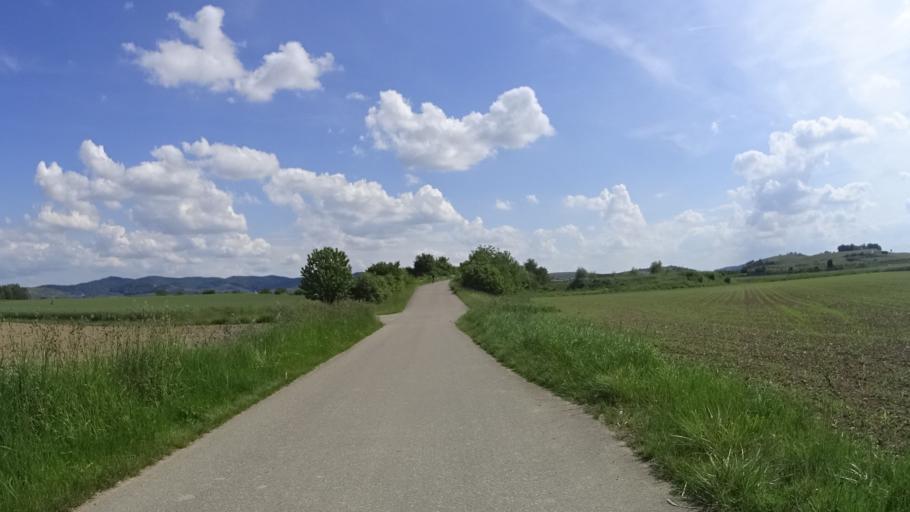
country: DE
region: Baden-Wuerttemberg
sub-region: Freiburg Region
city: Sasbach
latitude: 48.1575
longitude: 7.6218
